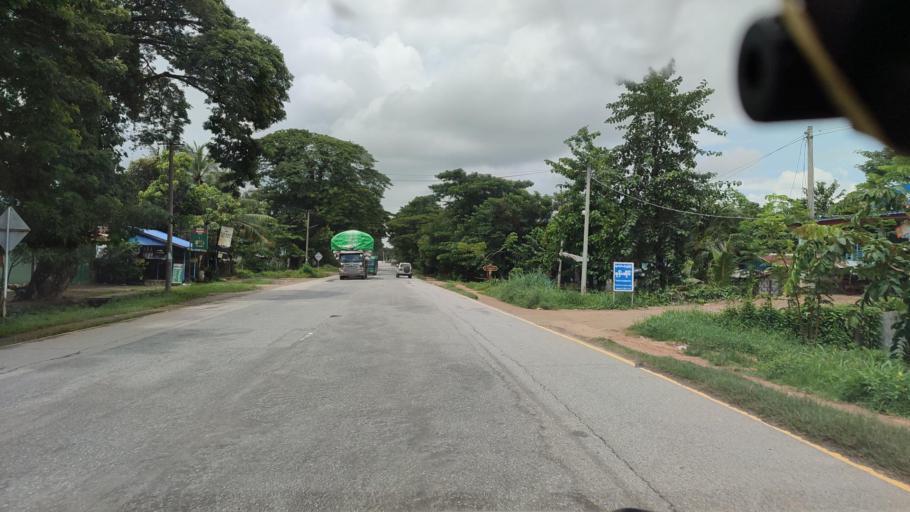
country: MM
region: Bago
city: Nyaunglebin
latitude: 17.6910
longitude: 96.5868
